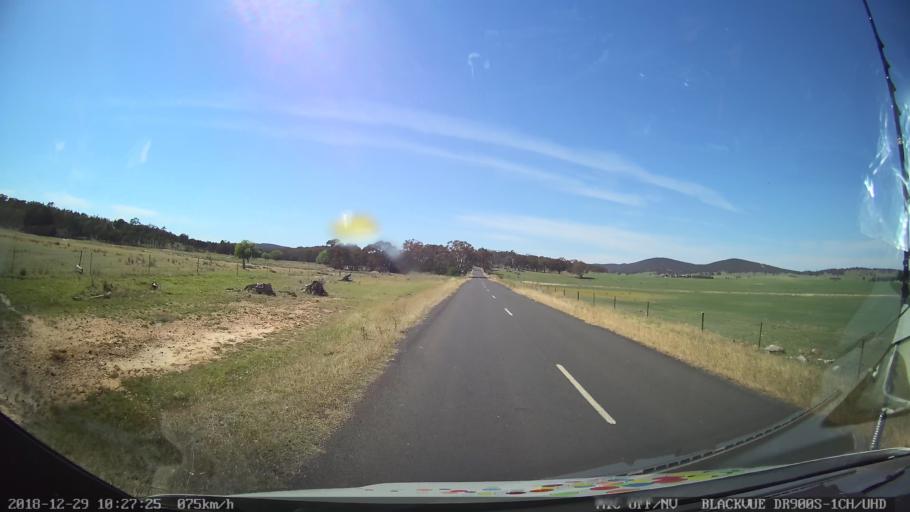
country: AU
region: New South Wales
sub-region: Yass Valley
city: Gundaroo
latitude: -34.9338
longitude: 149.4502
